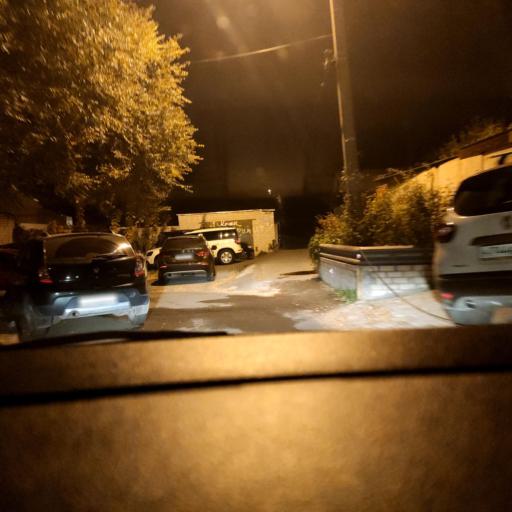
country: RU
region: Voronezj
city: Voronezh
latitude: 51.6408
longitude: 39.1656
